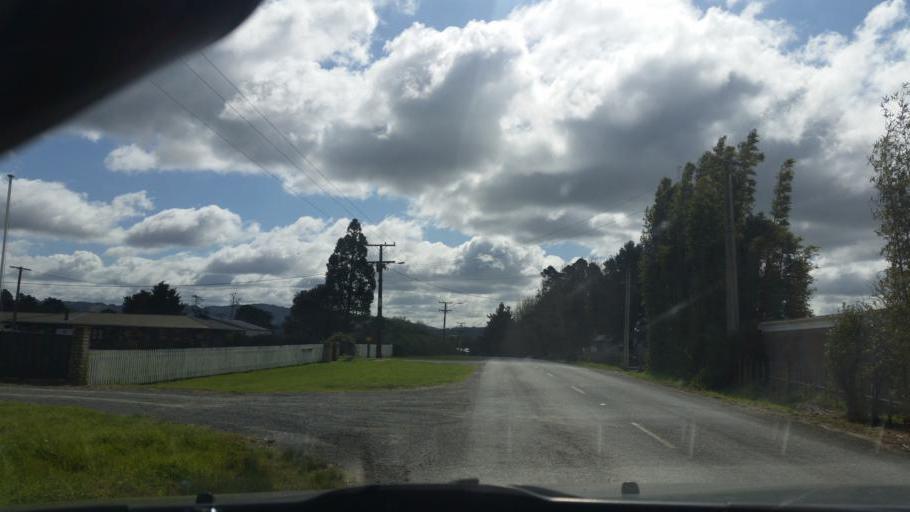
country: NZ
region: Auckland
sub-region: Auckland
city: Wellsford
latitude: -36.1434
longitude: 174.5084
